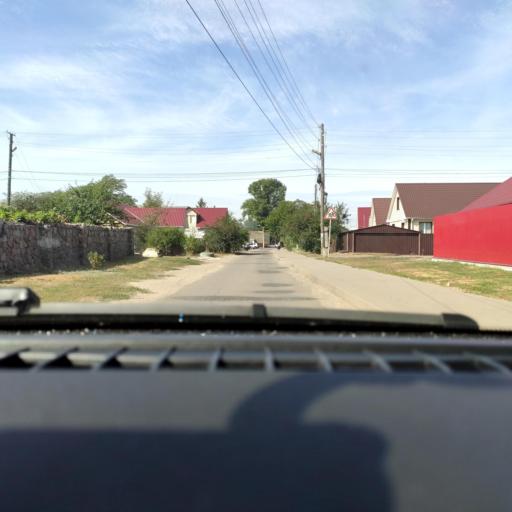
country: RU
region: Voronezj
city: Maslovka
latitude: 51.5511
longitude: 39.2409
